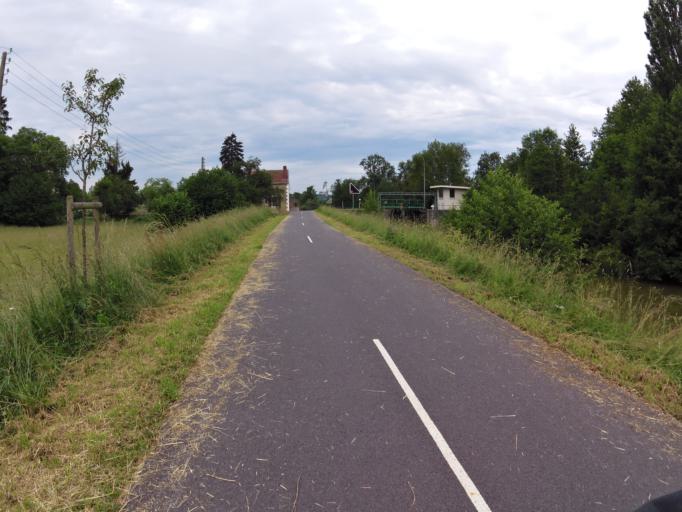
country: FR
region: Champagne-Ardenne
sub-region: Departement des Ardennes
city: Donchery
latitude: 49.6927
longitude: 4.8703
